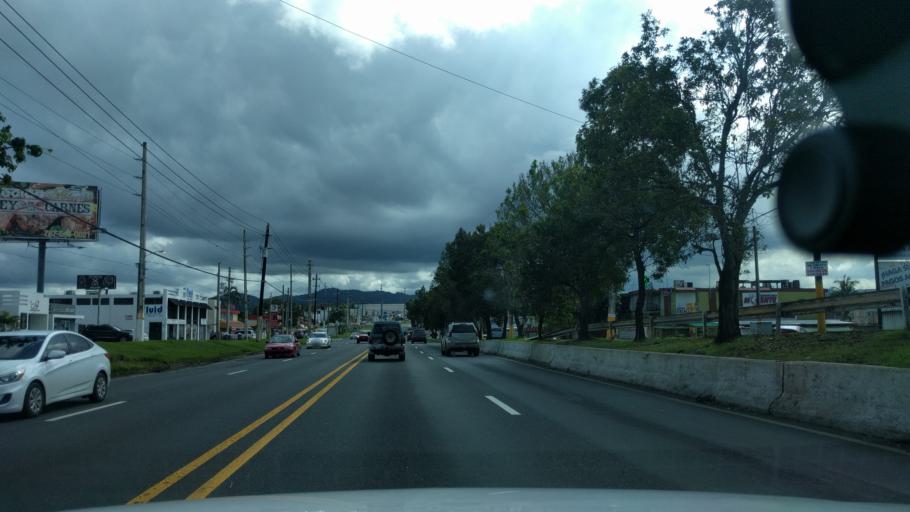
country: PR
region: Toa Alta
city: Pajaros
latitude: 18.3531
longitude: -66.1890
